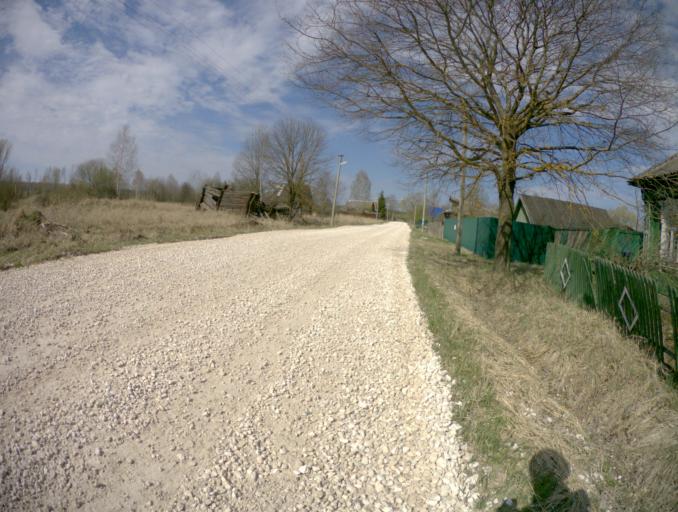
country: RU
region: Vladimir
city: Mezinovskiy
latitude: 55.4928
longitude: 40.3496
